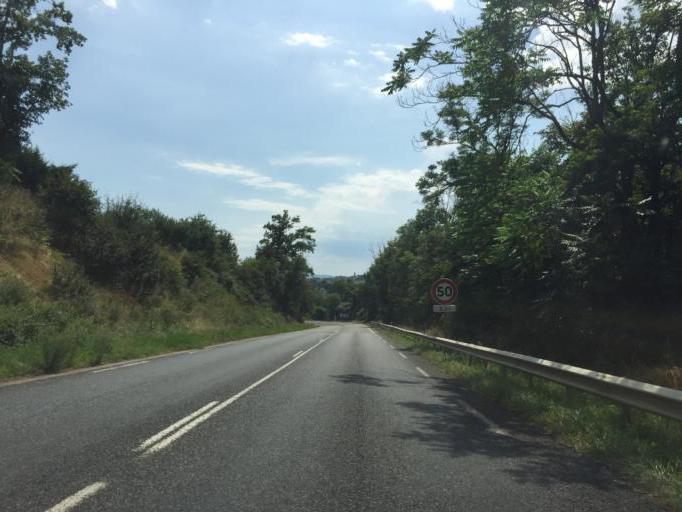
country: FR
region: Rhone-Alpes
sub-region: Departement du Rhone
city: Bully
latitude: 45.8456
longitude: 4.5795
